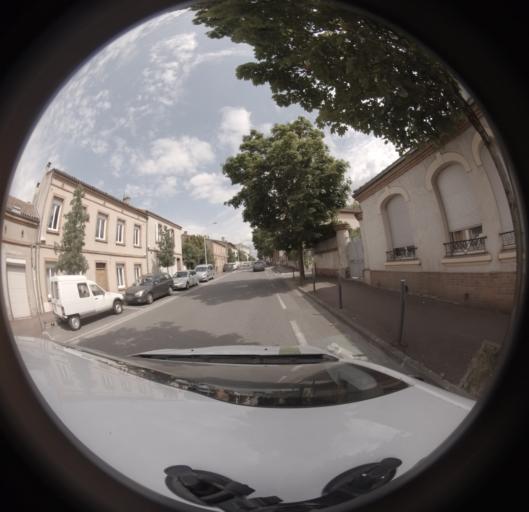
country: FR
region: Midi-Pyrenees
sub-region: Departement du Tarn-et-Garonne
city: Montauban
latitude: 44.0118
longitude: 1.3641
